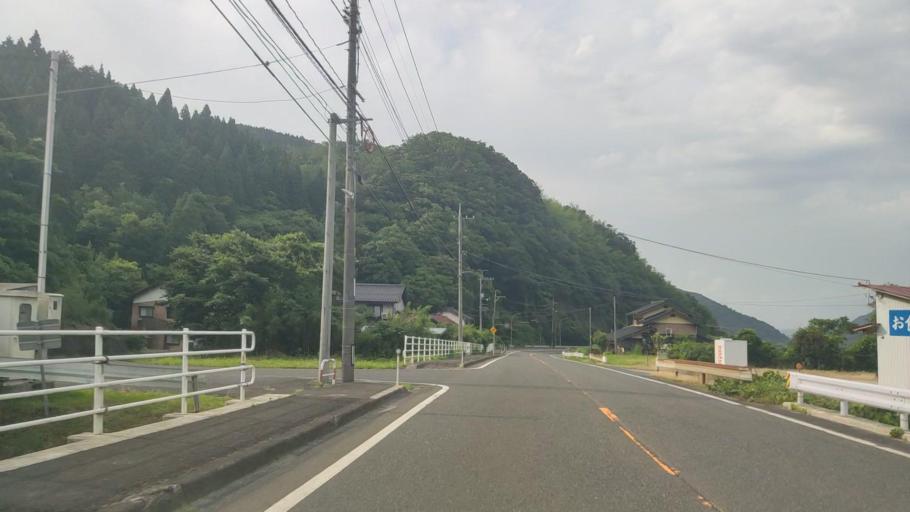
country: JP
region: Tottori
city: Kurayoshi
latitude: 35.3388
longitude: 133.8403
